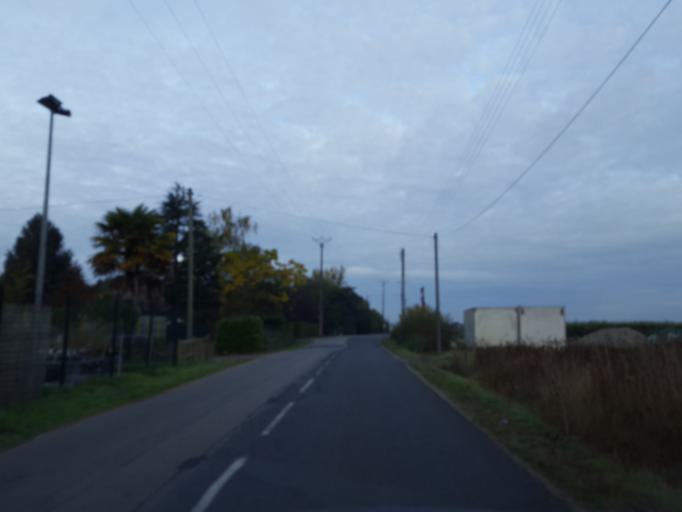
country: FR
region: Pays de la Loire
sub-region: Departement de la Loire-Atlantique
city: Saint-Julien-de-Concelles
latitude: 47.2460
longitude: -1.3986
